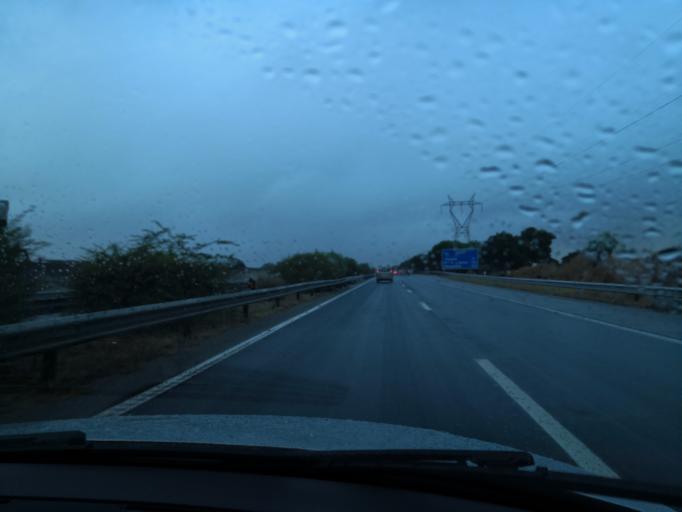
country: PT
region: Setubal
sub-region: Moita
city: Moita
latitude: 38.6495
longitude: -8.9706
